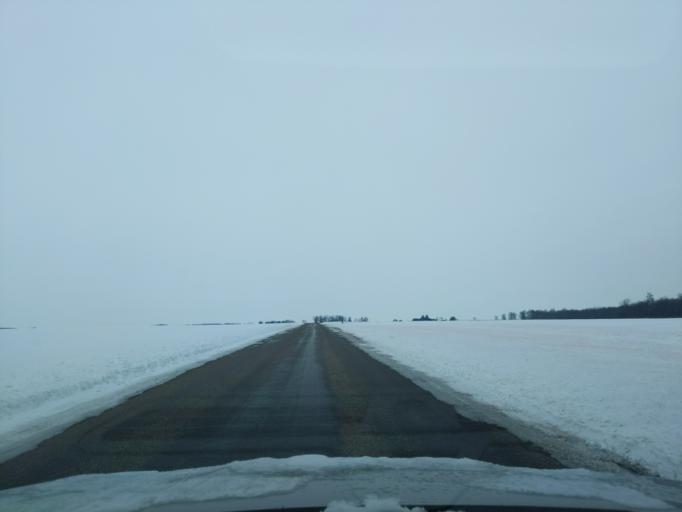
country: US
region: Indiana
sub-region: Benton County
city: Otterbein
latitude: 40.4304
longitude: -87.0927
